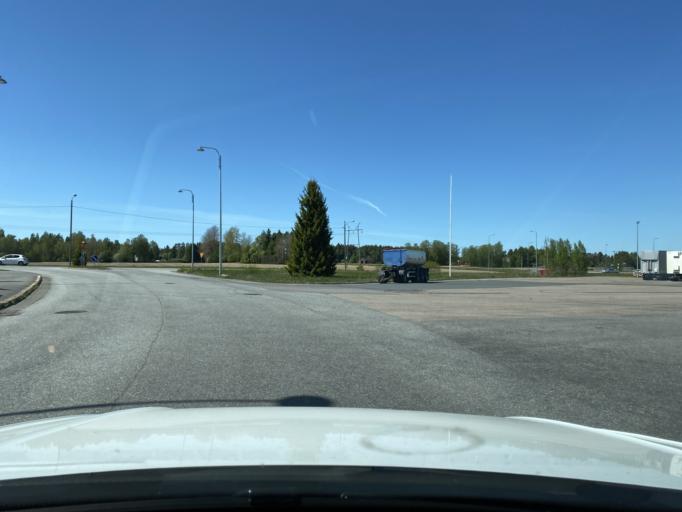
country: FI
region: Satakunta
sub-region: Rauma
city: Eura
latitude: 61.1300
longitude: 22.1265
